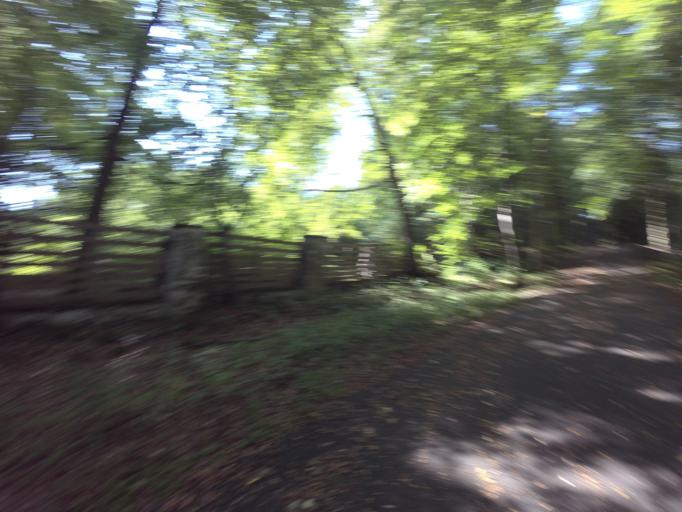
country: CZ
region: Jihocesky
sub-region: Okres Ceske Budejovice
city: Hluboka nad Vltavou
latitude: 49.0860
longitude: 14.4669
